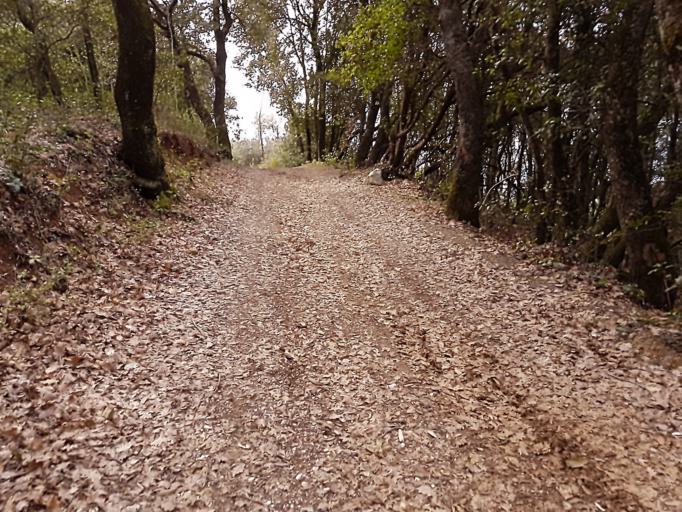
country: IT
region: Umbria
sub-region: Provincia di Perugia
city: Corciano
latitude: 43.1330
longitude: 12.3053
